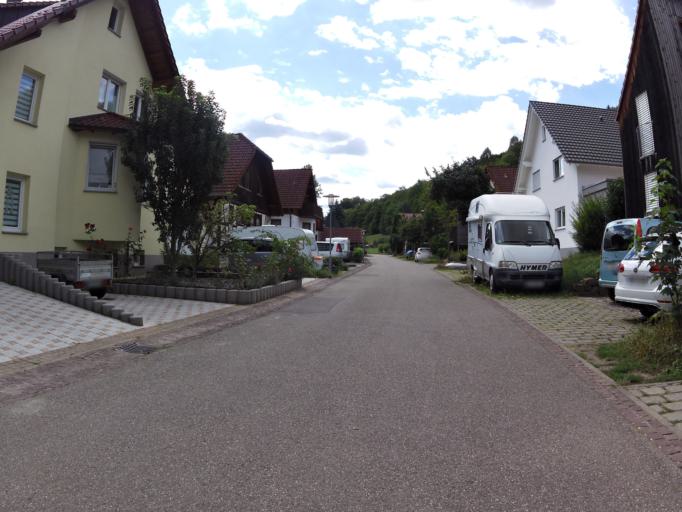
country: DE
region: Baden-Wuerttemberg
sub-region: Freiburg Region
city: Kippenheim
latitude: 48.3063
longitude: 7.8560
